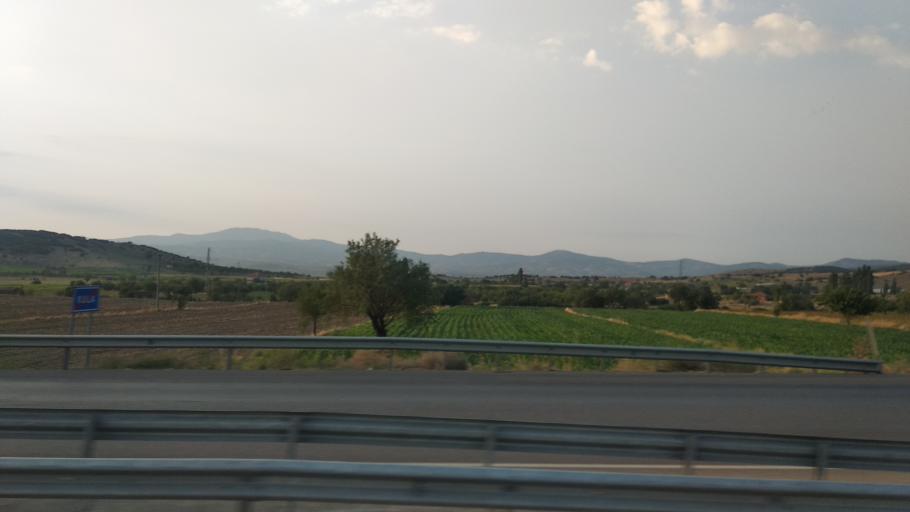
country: TR
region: Manisa
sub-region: Kula
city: Kula
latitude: 38.5517
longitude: 28.6831
